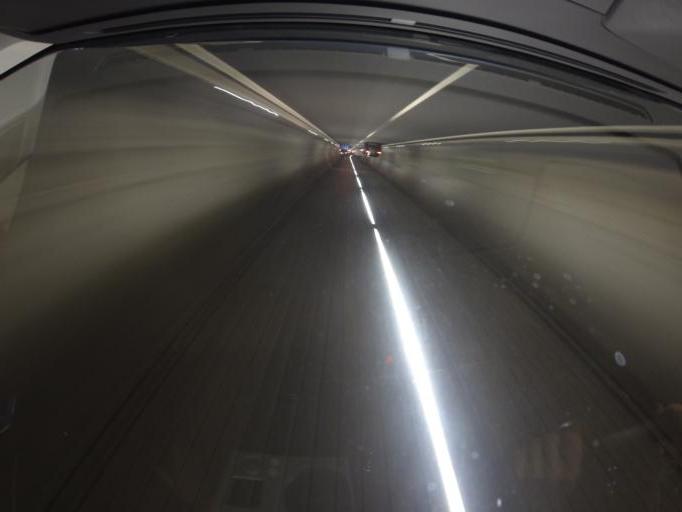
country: CH
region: Saint Gallen
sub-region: Wahlkreis See-Gaster
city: Weesen
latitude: 47.1243
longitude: 9.1187
